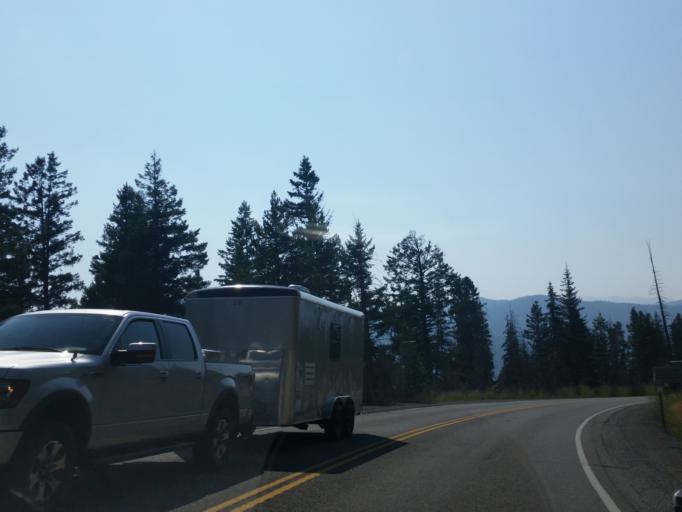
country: CA
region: British Columbia
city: Princeton
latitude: 49.2252
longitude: -120.5466
